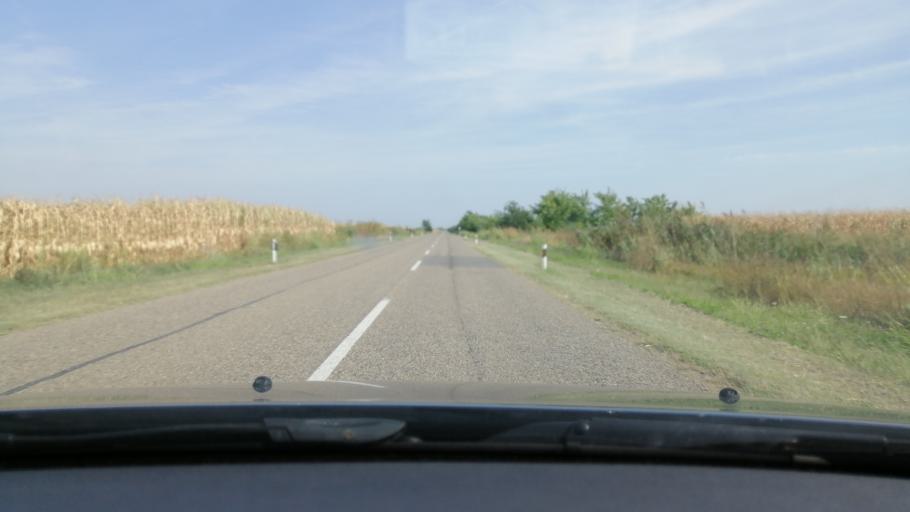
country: RS
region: Autonomna Pokrajina Vojvodina
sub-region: Juznobanatski Okrug
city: Kovacica
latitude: 45.1557
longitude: 20.6169
